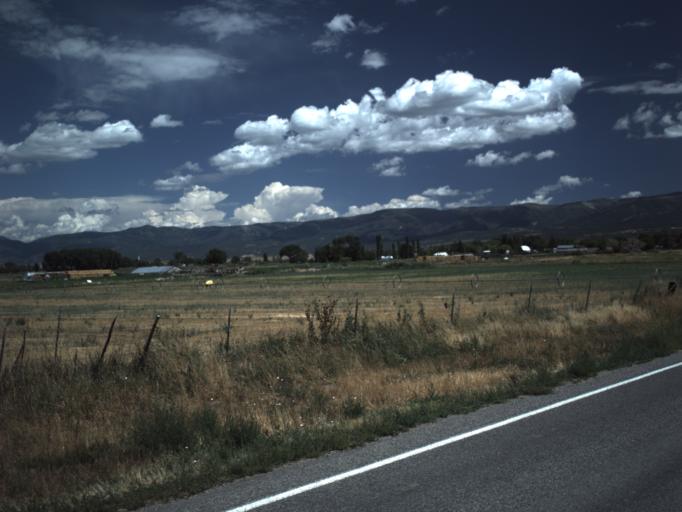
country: US
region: Utah
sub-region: Sanpete County
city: Mount Pleasant
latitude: 39.4818
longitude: -111.5053
